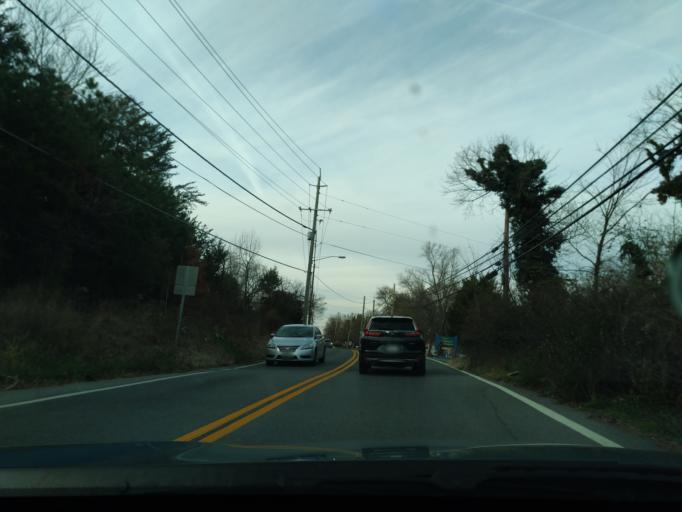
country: US
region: Maryland
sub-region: Prince George's County
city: Clinton
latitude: 38.7588
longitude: -76.8953
